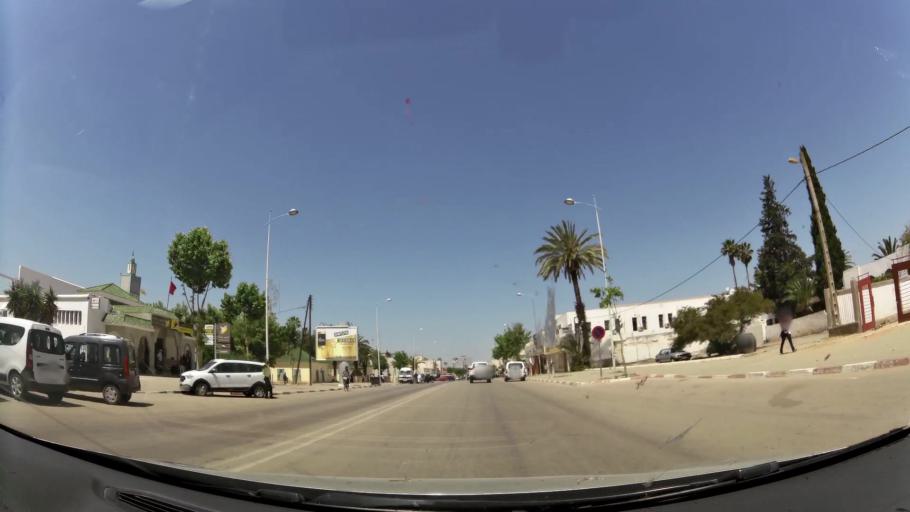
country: MA
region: Rabat-Sale-Zemmour-Zaer
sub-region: Khemisset
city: Khemisset
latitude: 33.8247
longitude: -6.0649
